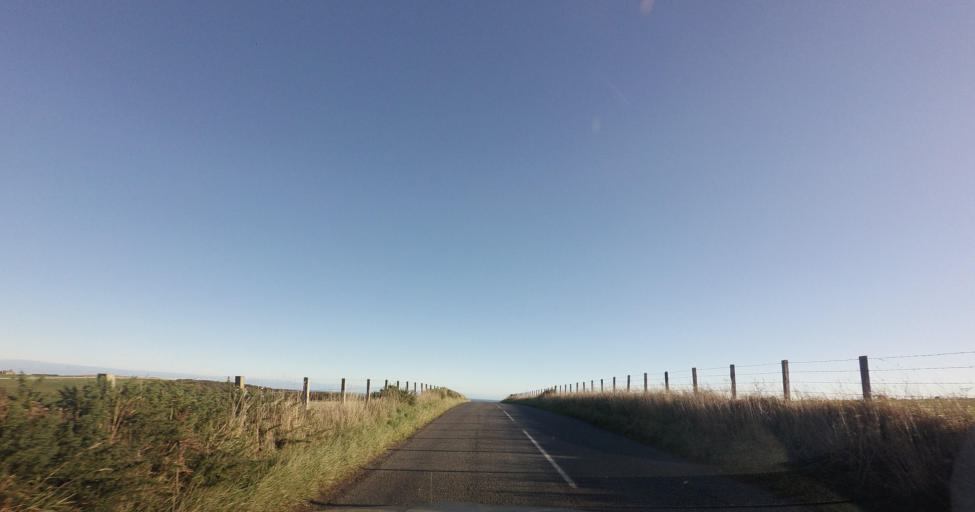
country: GB
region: Scotland
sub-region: Aberdeenshire
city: Rosehearty
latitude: 57.6734
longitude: -2.2978
